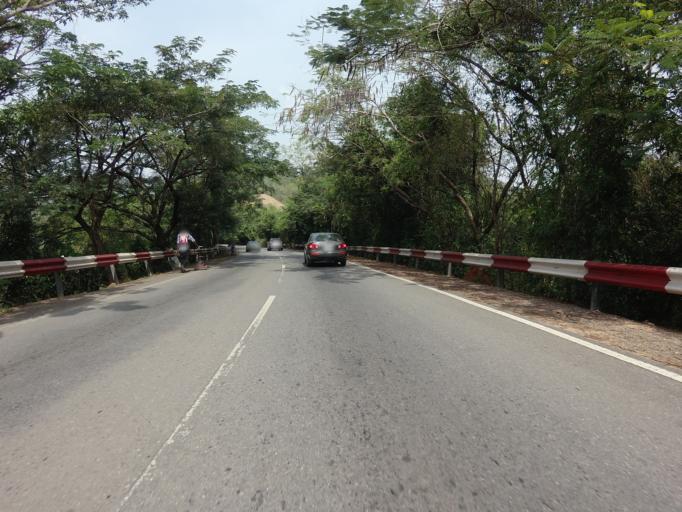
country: GH
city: Akropong
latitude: 6.2695
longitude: 0.0582
